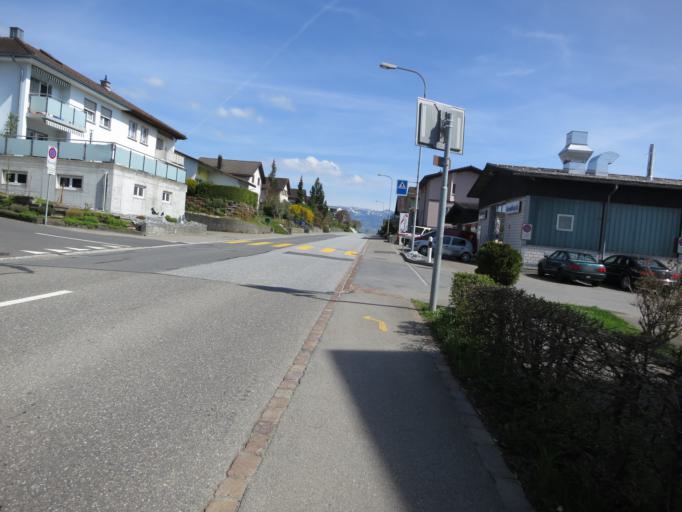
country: CH
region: Saint Gallen
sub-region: Wahlkreis See-Gaster
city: Eschenbach
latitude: 47.2418
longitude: 8.9138
